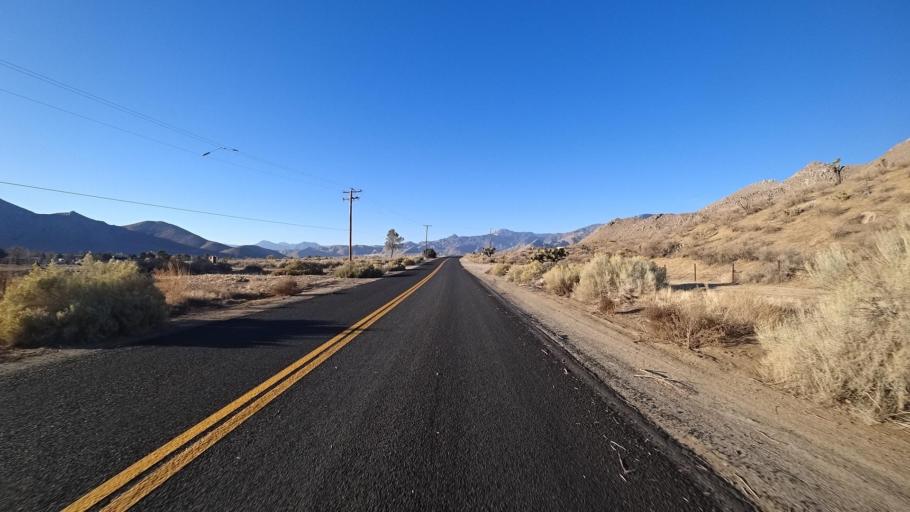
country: US
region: California
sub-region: Kern County
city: Weldon
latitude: 35.6352
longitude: -118.2448
